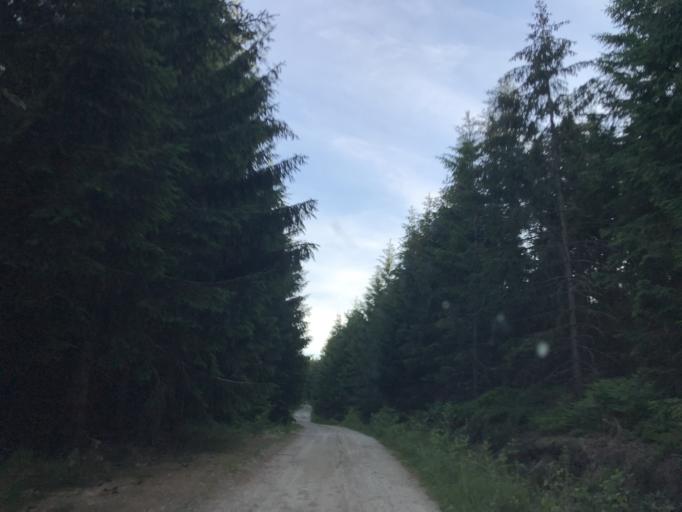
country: FR
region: Rhone-Alpes
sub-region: Departement de la Loire
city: Noiretable
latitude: 45.8080
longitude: 3.7039
